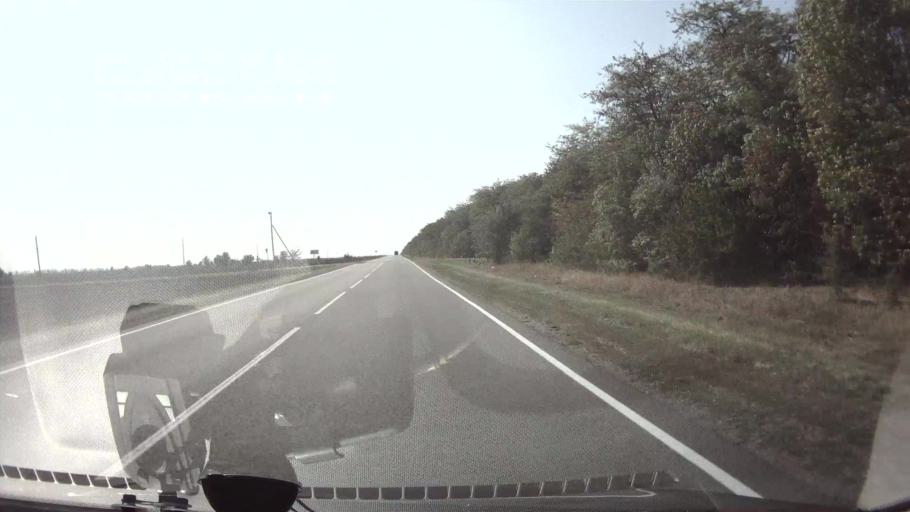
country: RU
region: Krasnodarskiy
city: Novopokrovskaya
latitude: 45.8808
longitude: 40.7208
